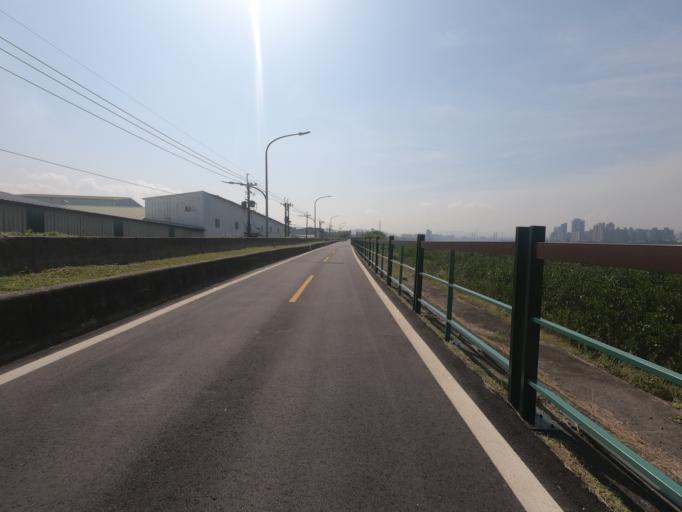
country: TW
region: Taipei
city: Taipei
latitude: 25.1037
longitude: 121.4812
